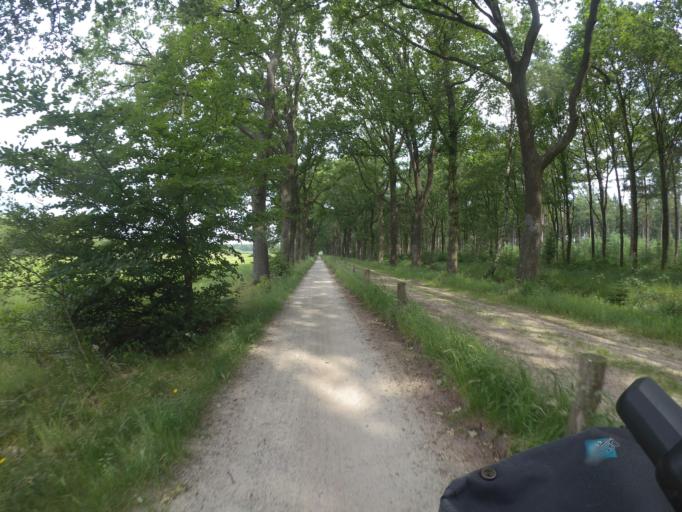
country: NL
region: Drenthe
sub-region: Gemeente Assen
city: Assen
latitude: 53.0085
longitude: 6.4408
